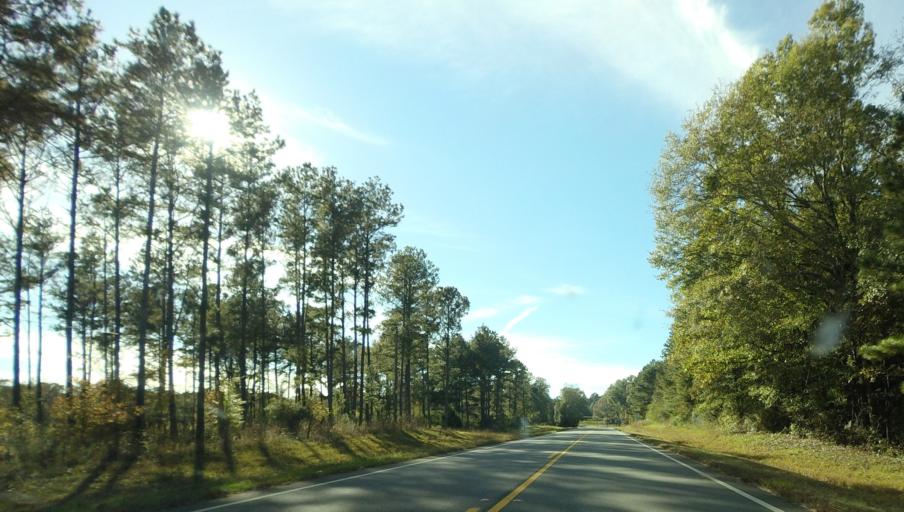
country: US
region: Georgia
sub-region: Talbot County
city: Talbotton
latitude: 32.6888
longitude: -84.5280
